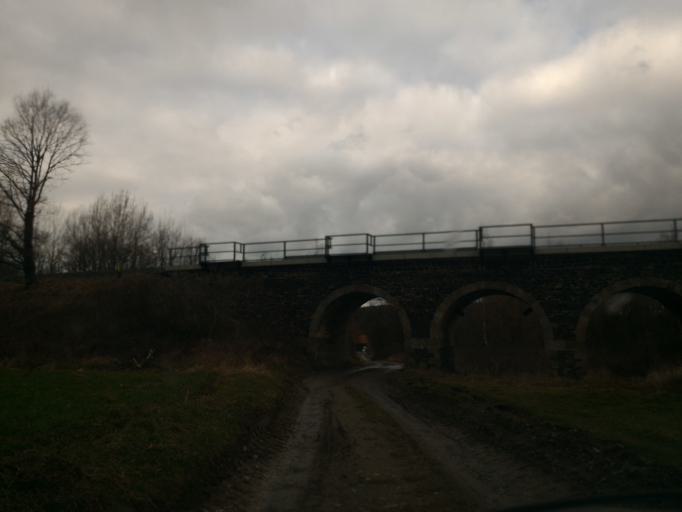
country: DE
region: Saxony
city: Grossschonau
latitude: 50.8896
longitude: 14.6856
